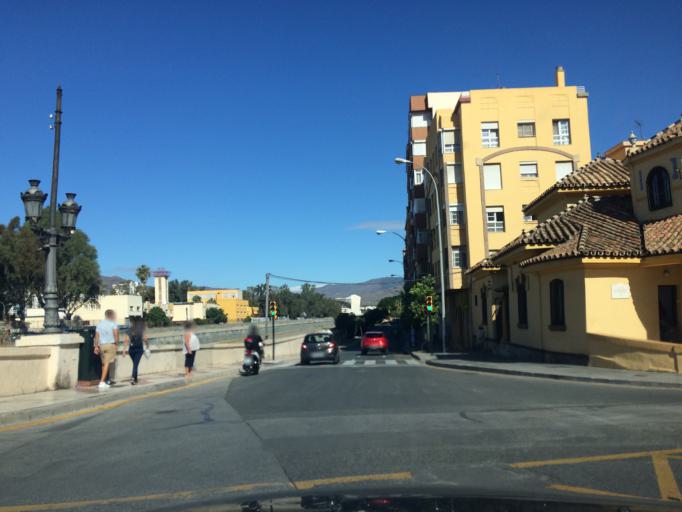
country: ES
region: Andalusia
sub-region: Provincia de Malaga
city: Malaga
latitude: 36.7268
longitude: -4.4256
